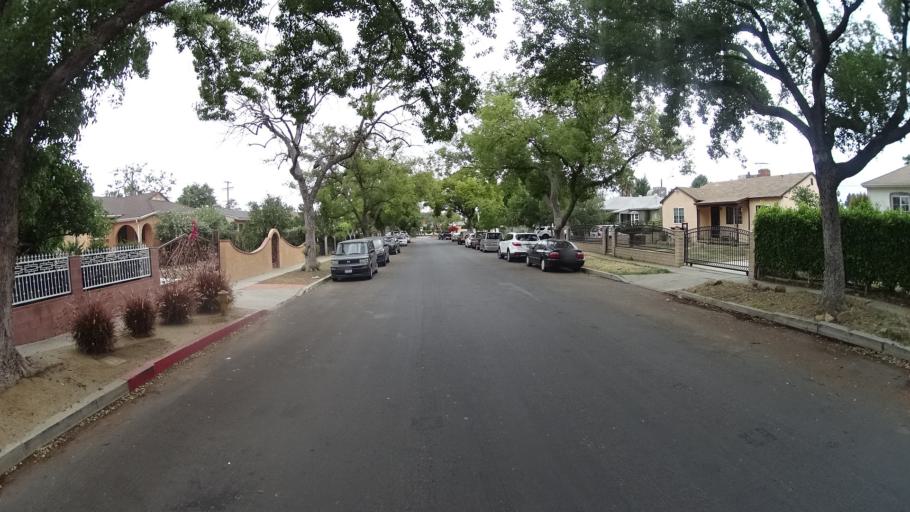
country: US
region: California
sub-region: Los Angeles County
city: San Fernando
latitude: 34.2498
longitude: -118.4473
